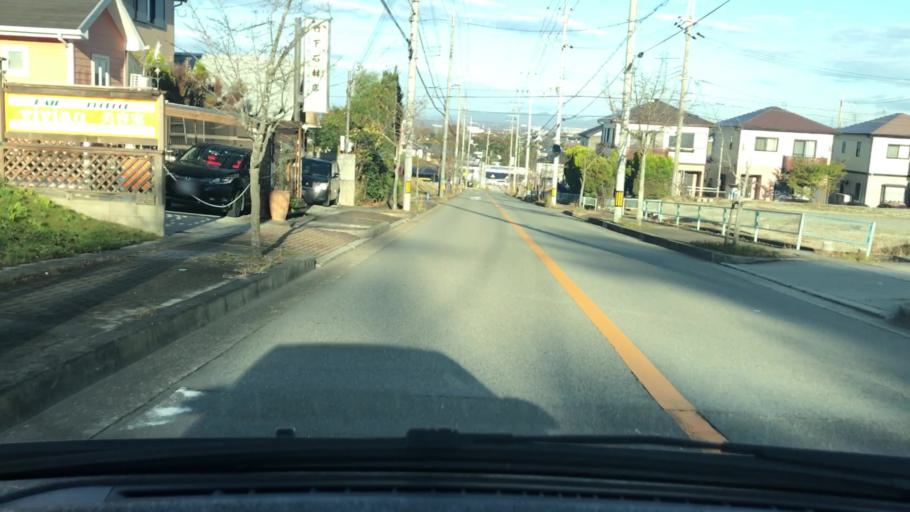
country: JP
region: Hyogo
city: Sandacho
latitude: 34.8255
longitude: 135.2515
